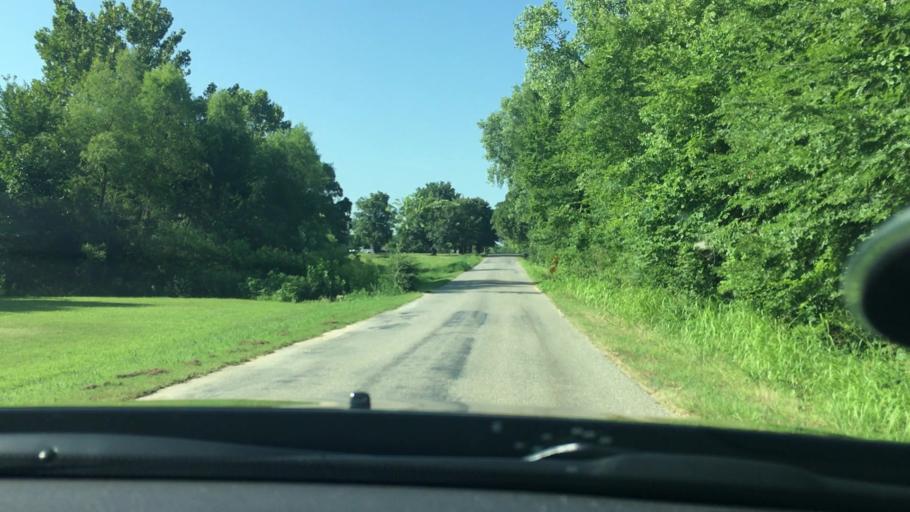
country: US
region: Oklahoma
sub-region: Pontotoc County
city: Byng
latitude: 34.8191
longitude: -96.6259
